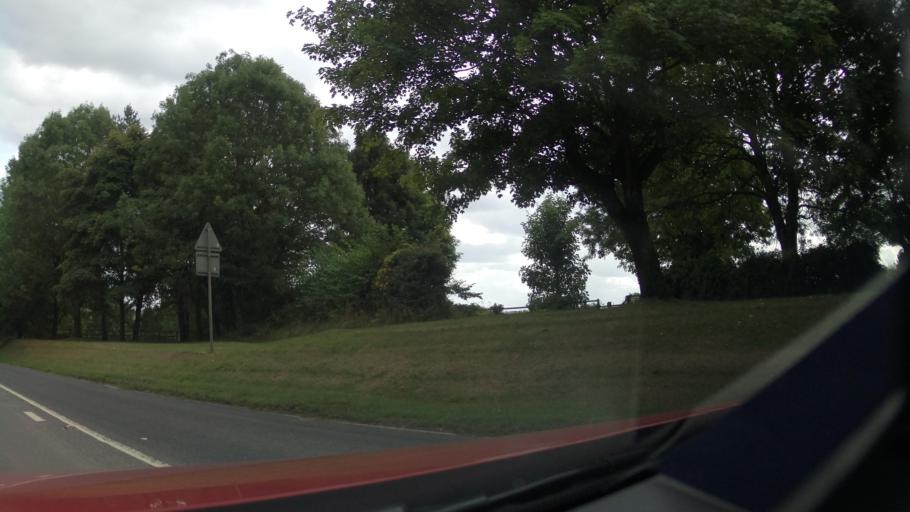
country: GB
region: England
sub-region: North Yorkshire
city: Ripon
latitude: 54.1783
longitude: -1.5566
